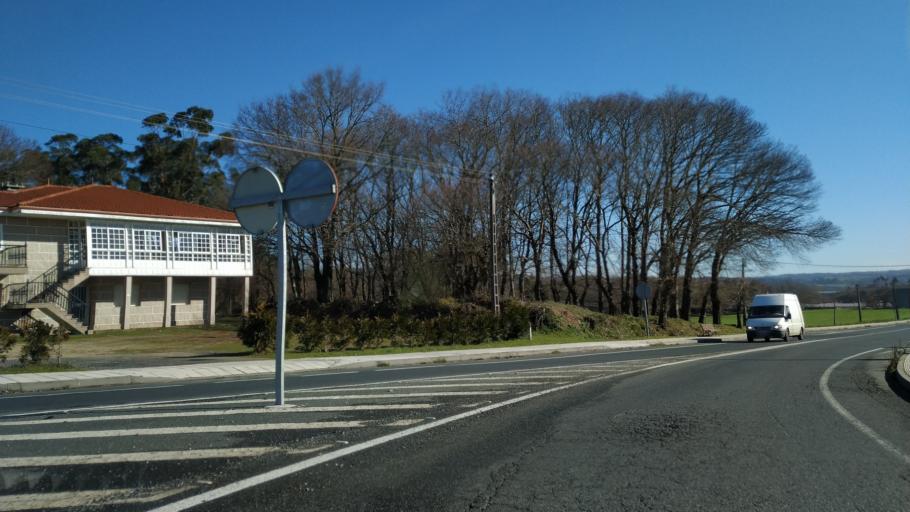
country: ES
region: Galicia
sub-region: Provincia de Pontevedra
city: Silleda
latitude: 42.6955
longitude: -8.2396
